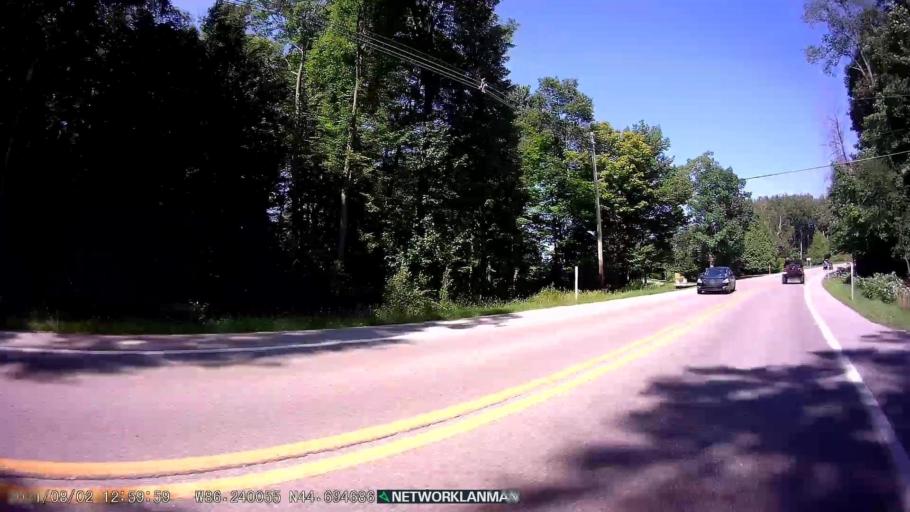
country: US
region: Michigan
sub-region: Benzie County
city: Frankfort
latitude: 44.6950
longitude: -86.2399
